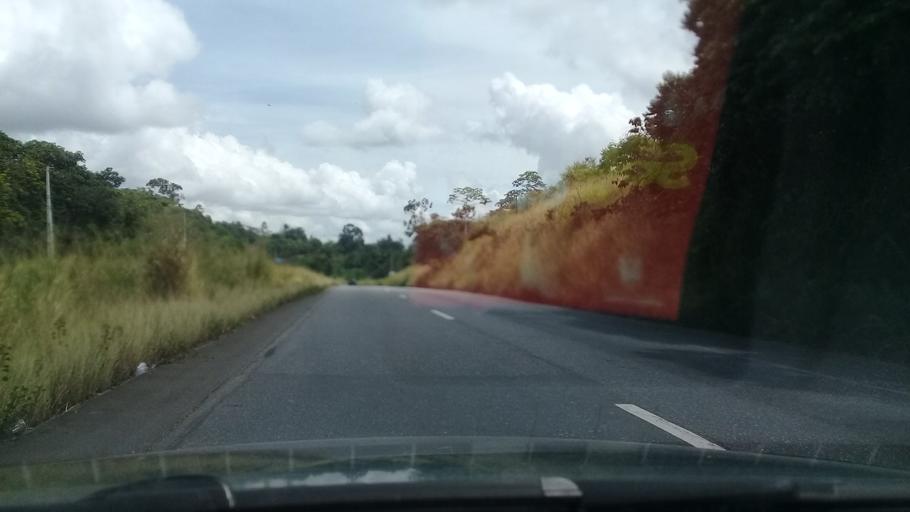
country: BR
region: Pernambuco
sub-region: Moreno
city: Moreno
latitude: -8.0991
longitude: -35.0966
